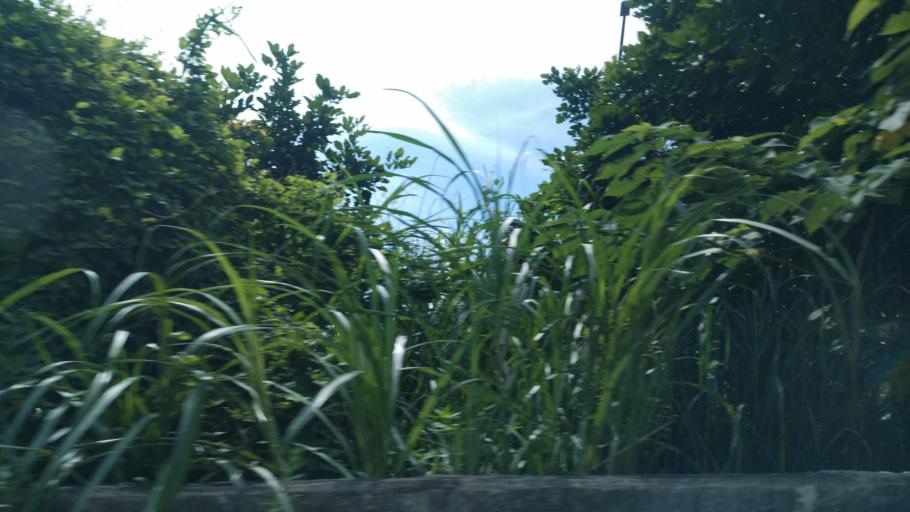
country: TW
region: Taipei
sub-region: Taipei
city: Banqiao
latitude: 24.9628
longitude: 121.5166
